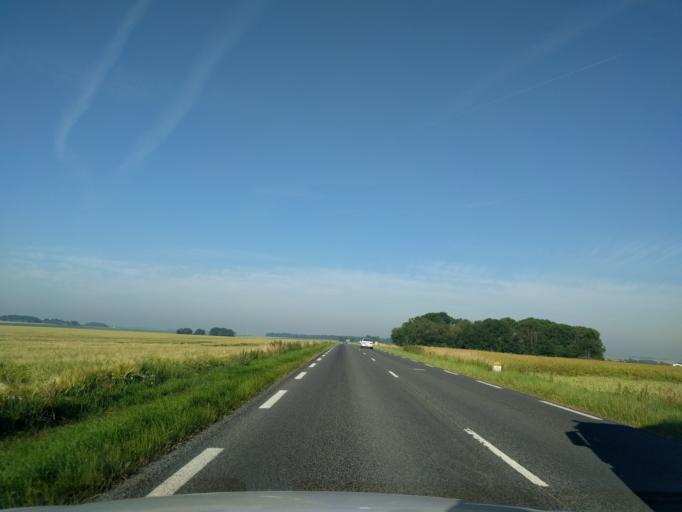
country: FR
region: Picardie
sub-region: Departement de la Somme
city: Roye
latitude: 49.6557
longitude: 2.6967
